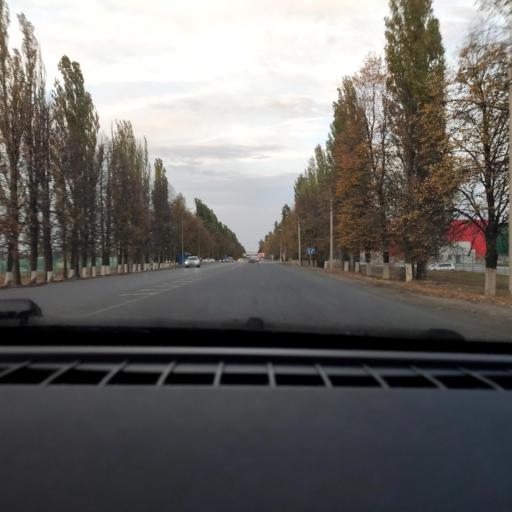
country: RU
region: Voronezj
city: Podgornoye
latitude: 51.8065
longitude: 39.2170
